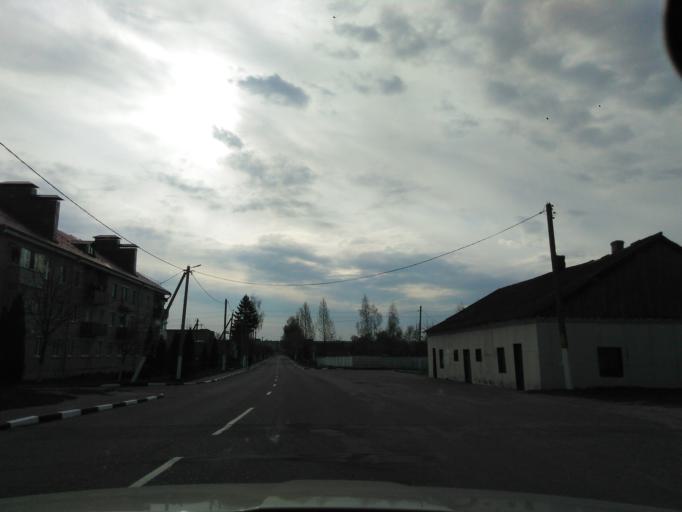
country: BY
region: Vitebsk
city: Chashniki
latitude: 54.8526
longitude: 29.1581
